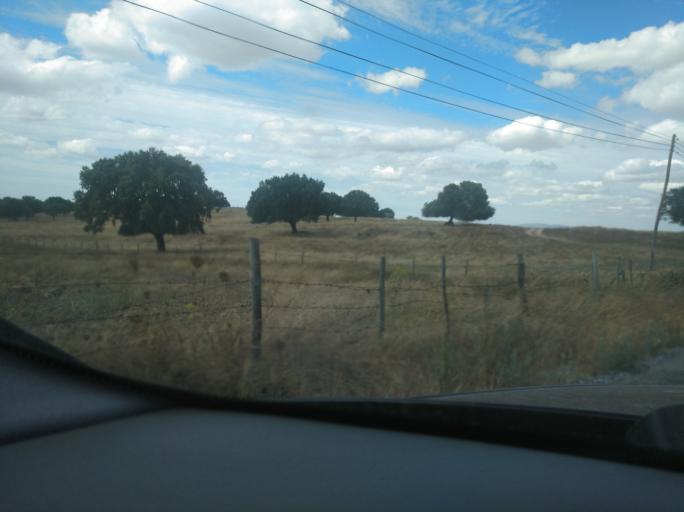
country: PT
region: Portalegre
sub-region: Arronches
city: Arronches
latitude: 39.0675
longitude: -7.4019
